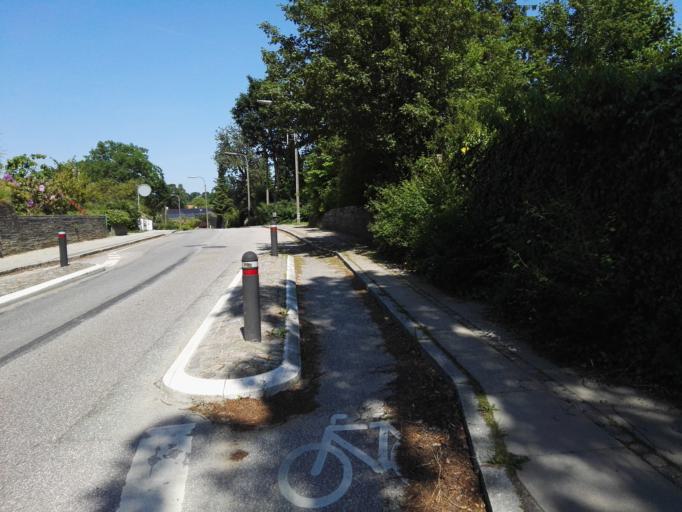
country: DK
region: Capital Region
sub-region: Fureso Kommune
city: Vaerlose
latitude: 55.7576
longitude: 12.3922
